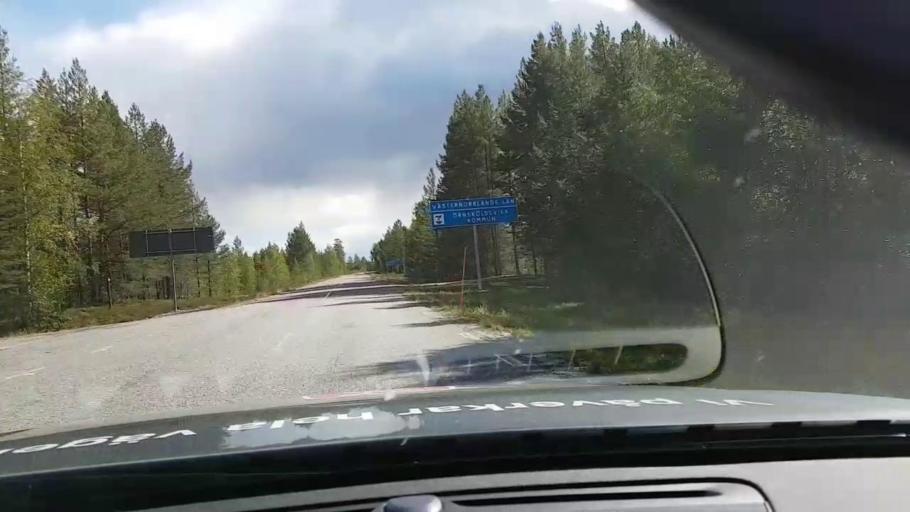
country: SE
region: Vaesterbotten
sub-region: Asele Kommun
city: Asele
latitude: 63.9074
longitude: 17.3415
